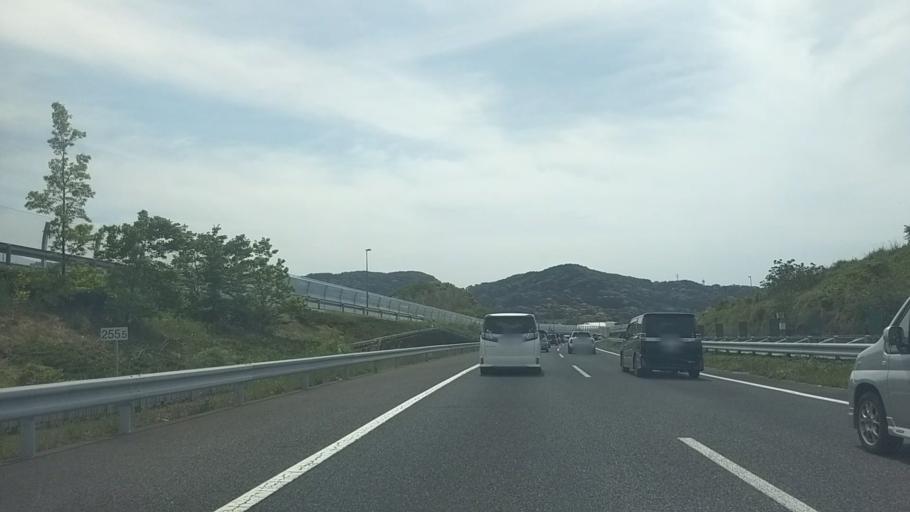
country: JP
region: Aichi
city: Shinshiro
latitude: 34.8246
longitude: 137.5472
